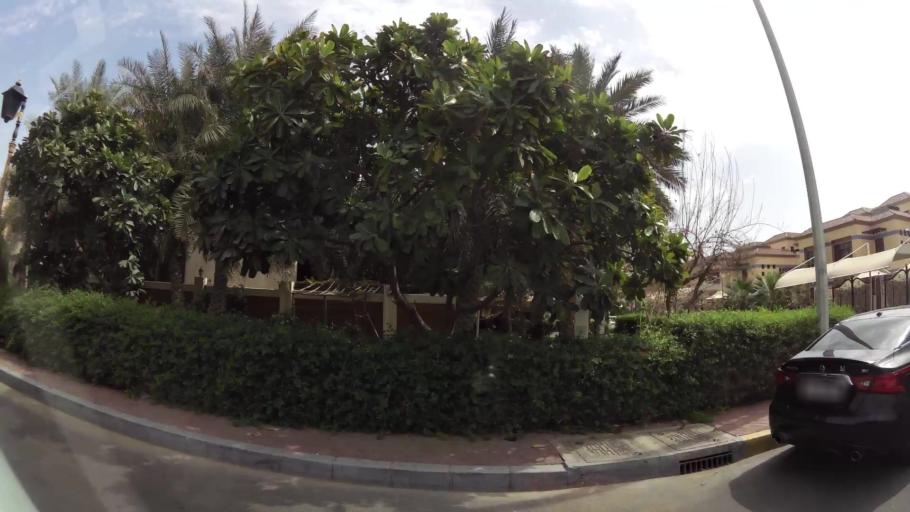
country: AE
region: Abu Dhabi
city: Abu Dhabi
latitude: 24.4575
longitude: 54.3671
